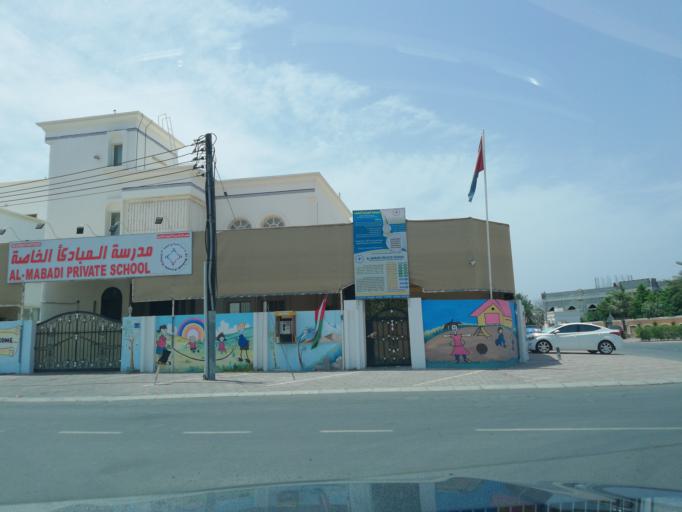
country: OM
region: Muhafazat Masqat
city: As Sib al Jadidah
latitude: 23.6586
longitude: 58.1979
